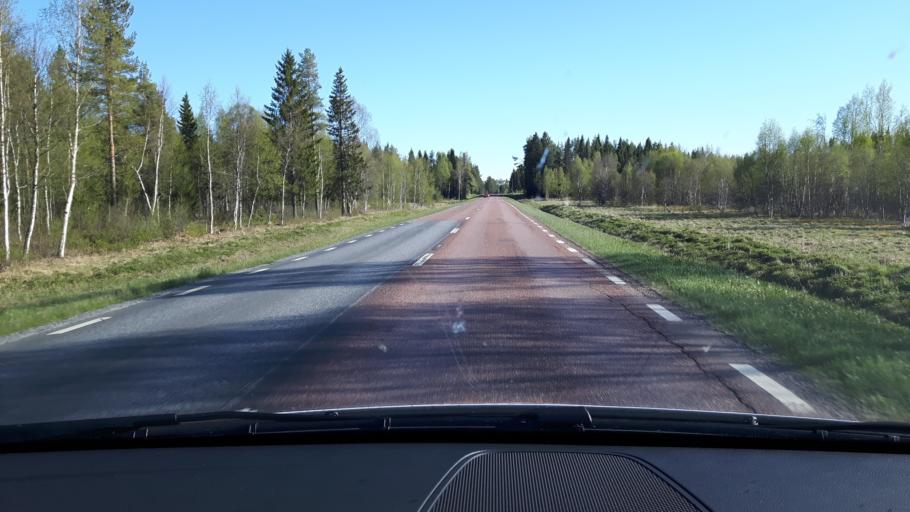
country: SE
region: Jaemtland
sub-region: Stroemsunds Kommun
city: Stroemsund
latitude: 63.7549
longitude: 15.4980
